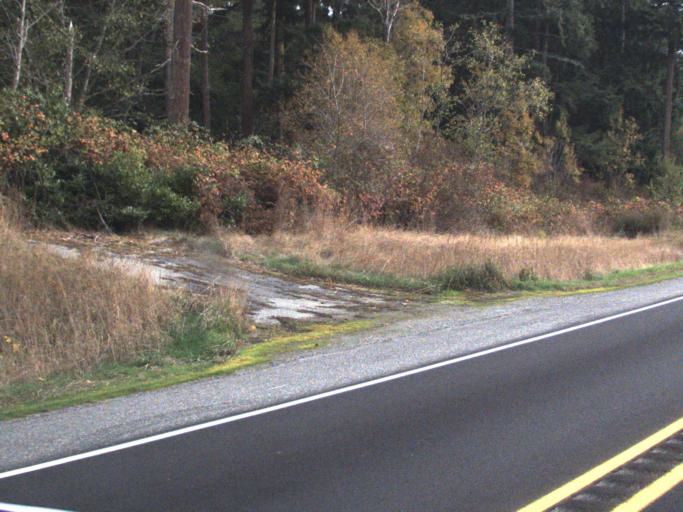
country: US
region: Washington
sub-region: Island County
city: Freeland
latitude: 48.0213
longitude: -122.5562
